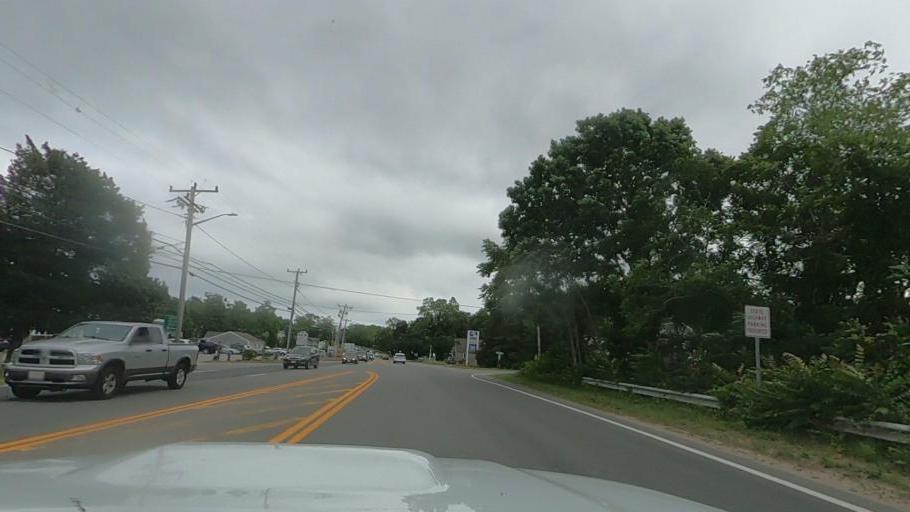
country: US
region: Massachusetts
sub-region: Barnstable County
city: Wellfleet
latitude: 41.9359
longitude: -70.0210
